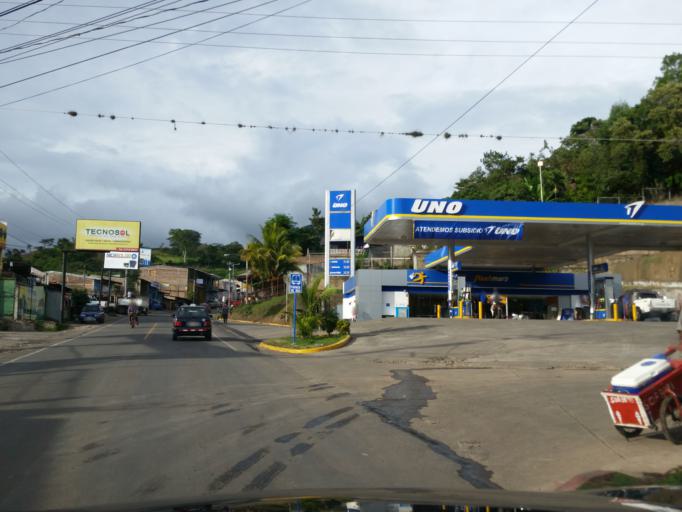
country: NI
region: Matagalpa
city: Matagalpa
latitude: 12.9384
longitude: -85.9069
